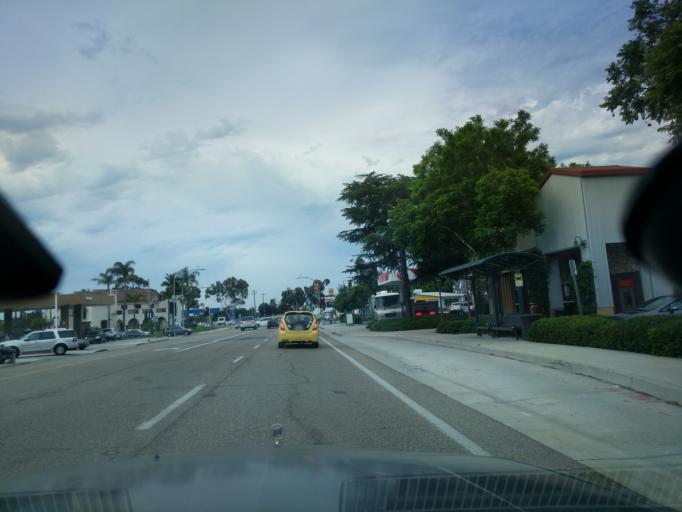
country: US
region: California
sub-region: Santa Barbara County
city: Goleta
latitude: 34.4426
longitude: -119.8307
